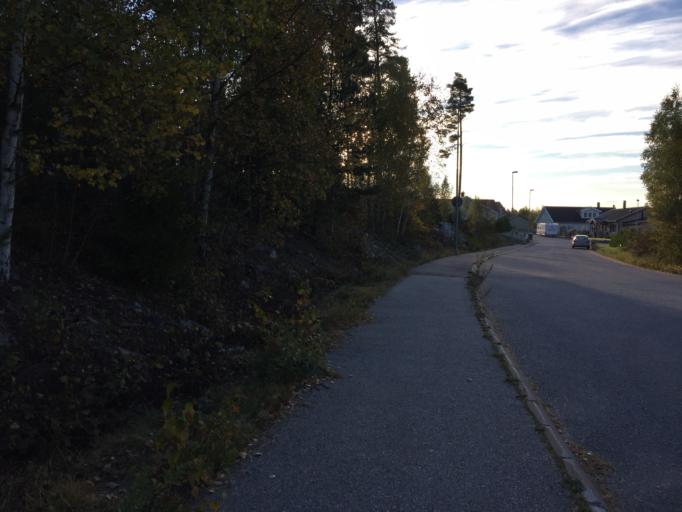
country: SE
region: Vaestmanland
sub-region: Hallstahammars Kommun
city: Hallstahammar
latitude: 59.6304
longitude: 16.2344
